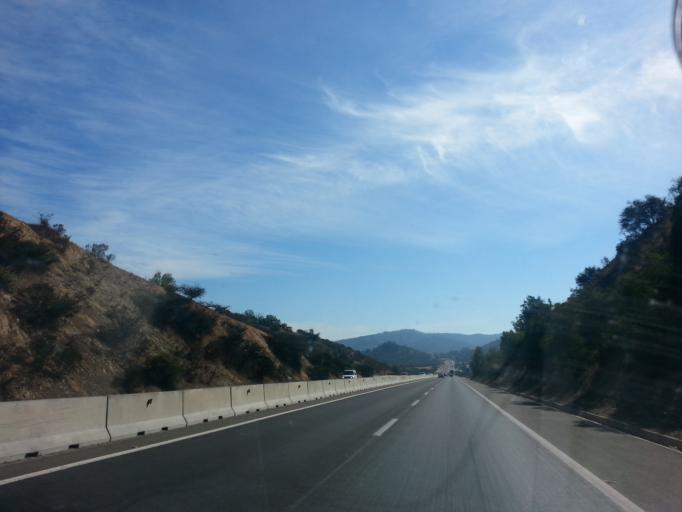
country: CL
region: Valparaiso
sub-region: Provincia de Marga Marga
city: Quilpue
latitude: -33.2802
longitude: -71.4279
